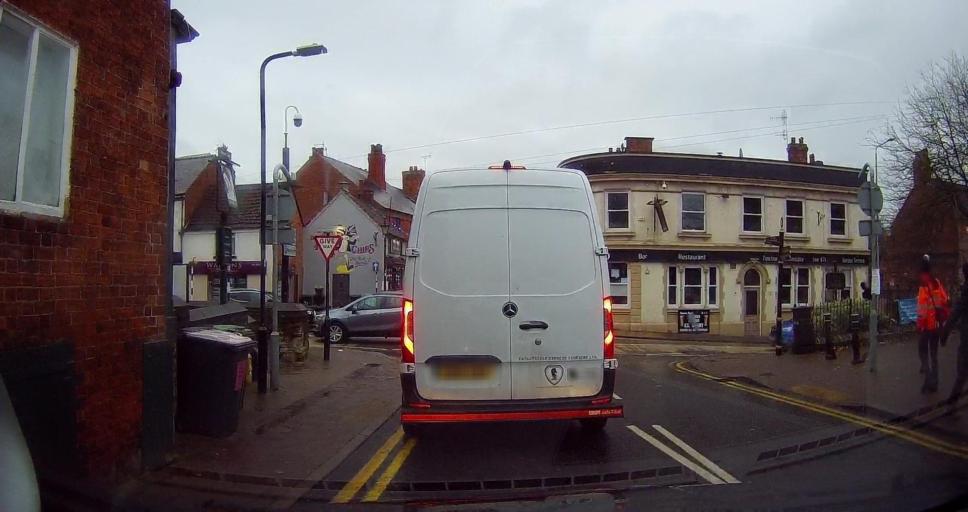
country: GB
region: England
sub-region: Nottinghamshire
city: Kimberley
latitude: 52.9977
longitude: -1.2570
